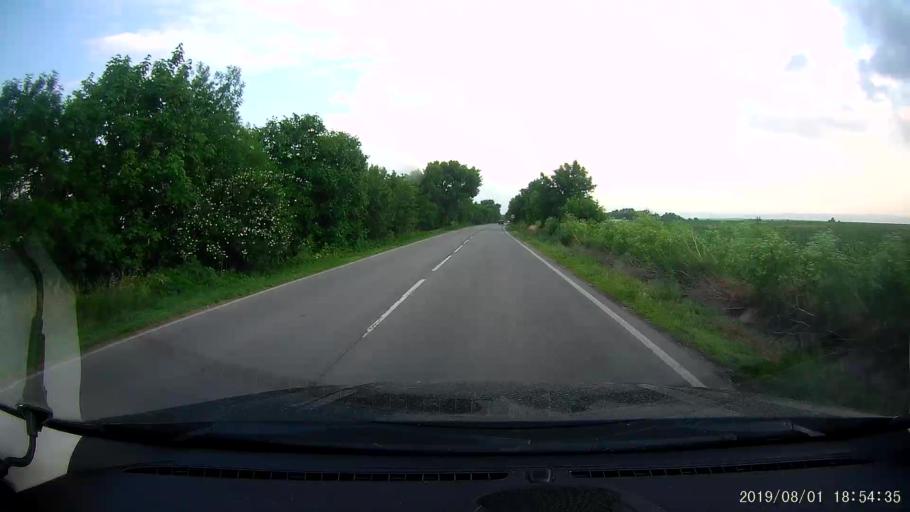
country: BG
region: Shumen
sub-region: Obshtina Shumen
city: Shumen
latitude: 43.1949
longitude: 27.0025
